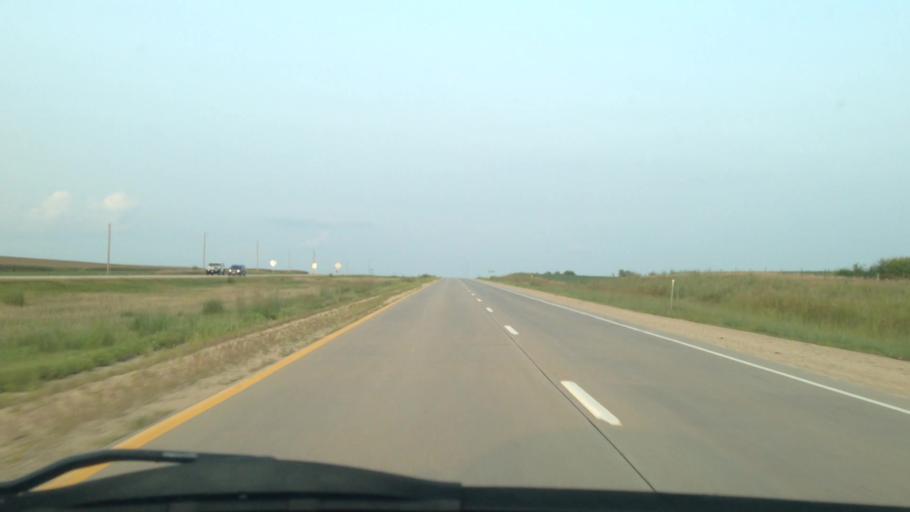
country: US
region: Iowa
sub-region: Benton County
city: Atkins
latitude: 41.9632
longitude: -91.9777
